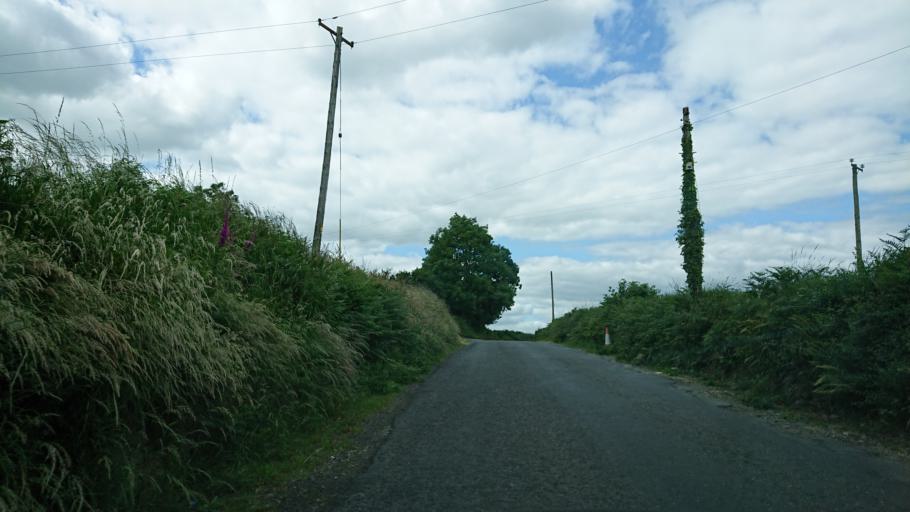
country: IE
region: Munster
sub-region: Waterford
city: Tra Mhor
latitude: 52.2108
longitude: -7.1691
